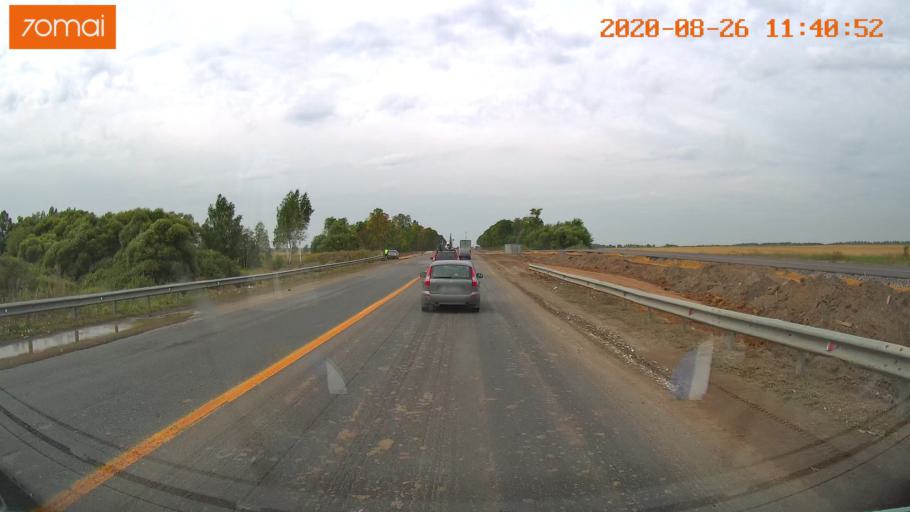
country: RU
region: Rjazan
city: Shilovo
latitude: 54.2949
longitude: 40.7199
